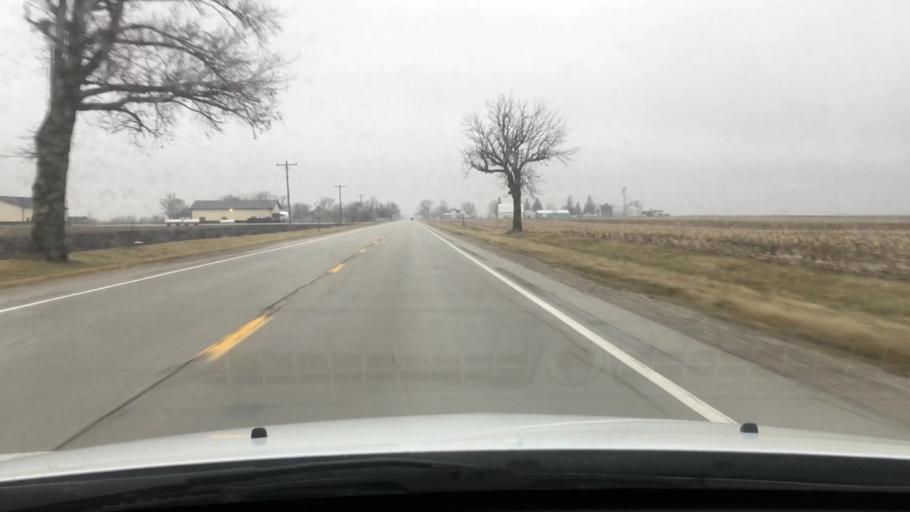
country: US
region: Illinois
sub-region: Livingston County
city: Flanagan
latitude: 40.8707
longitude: -88.8746
